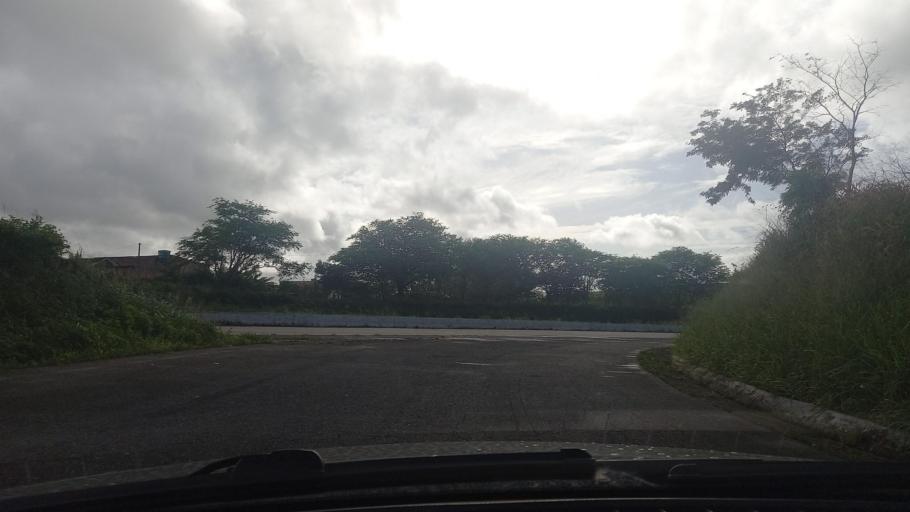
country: BR
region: Pernambuco
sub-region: Pombos
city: Pombos
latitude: -8.1289
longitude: -35.3527
